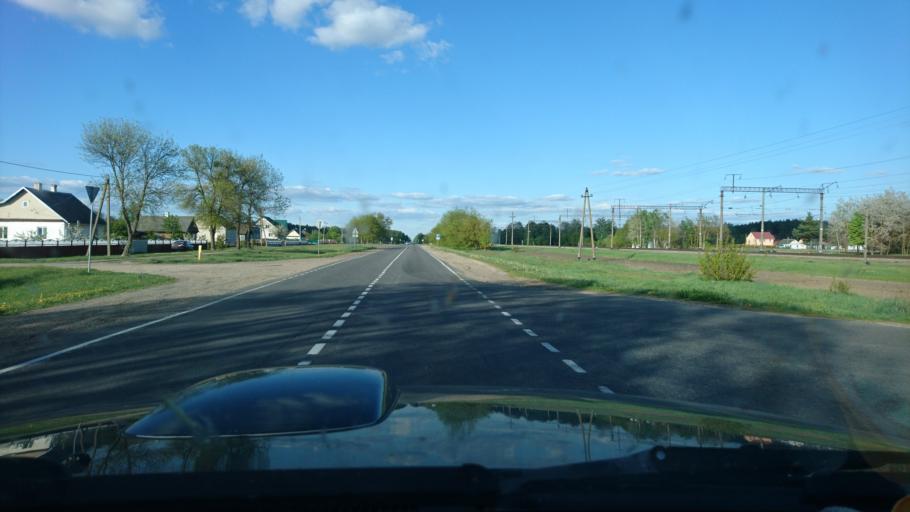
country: BY
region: Brest
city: Nyakhachava
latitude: 52.6485
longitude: 25.2148
